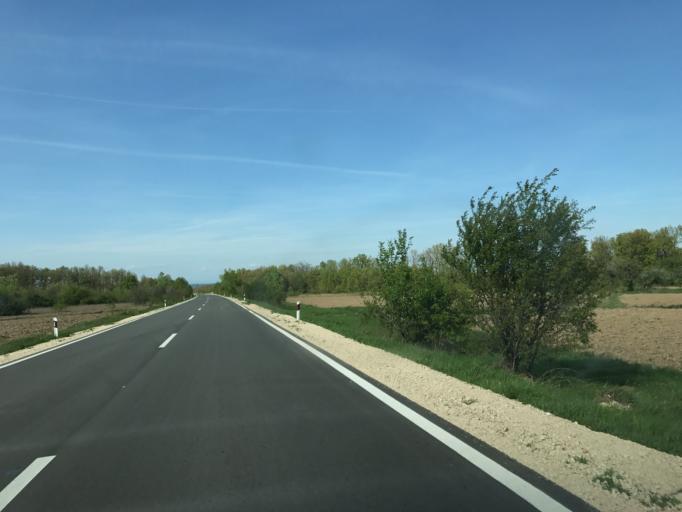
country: RS
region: Central Serbia
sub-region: Borski Okrug
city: Negotin
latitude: 44.1698
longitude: 22.3644
